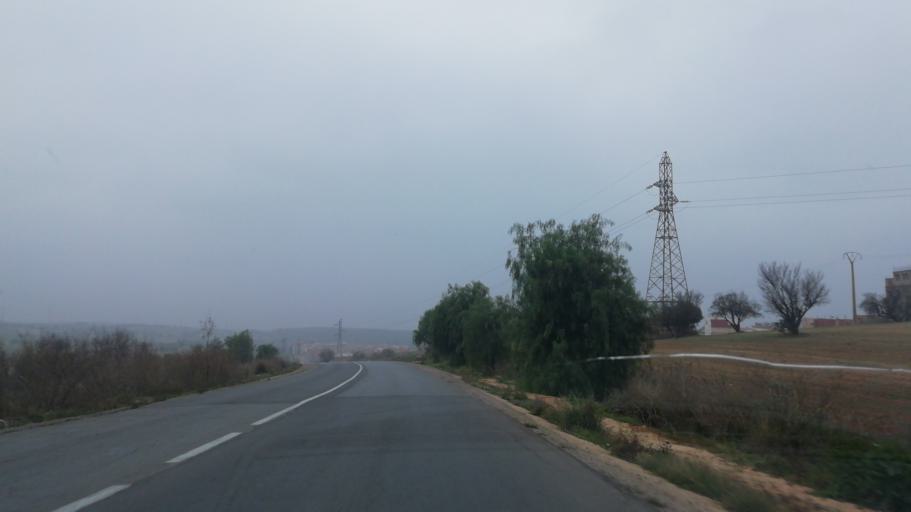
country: DZ
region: Mascara
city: Mascara
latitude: 35.4083
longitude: 0.1600
